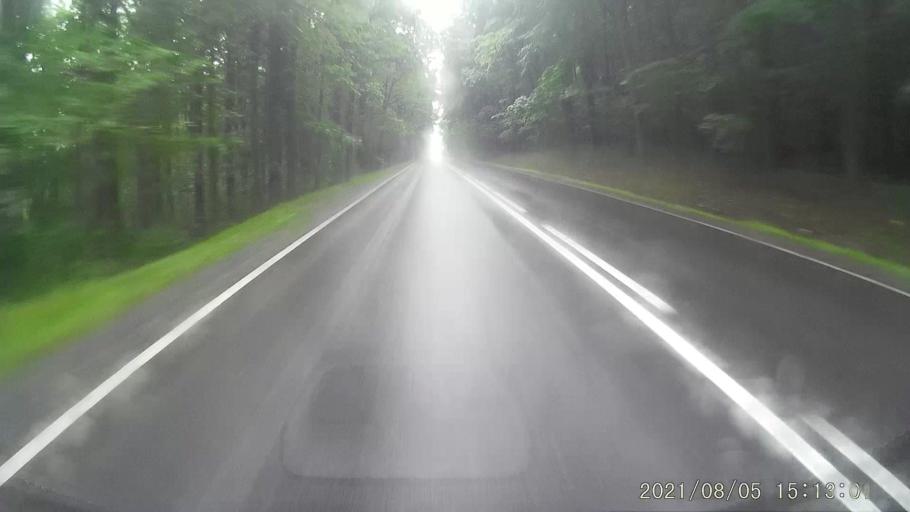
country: PL
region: Lower Silesian Voivodeship
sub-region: Powiat zabkowicki
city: Zloty Stok
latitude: 50.4496
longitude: 16.9043
